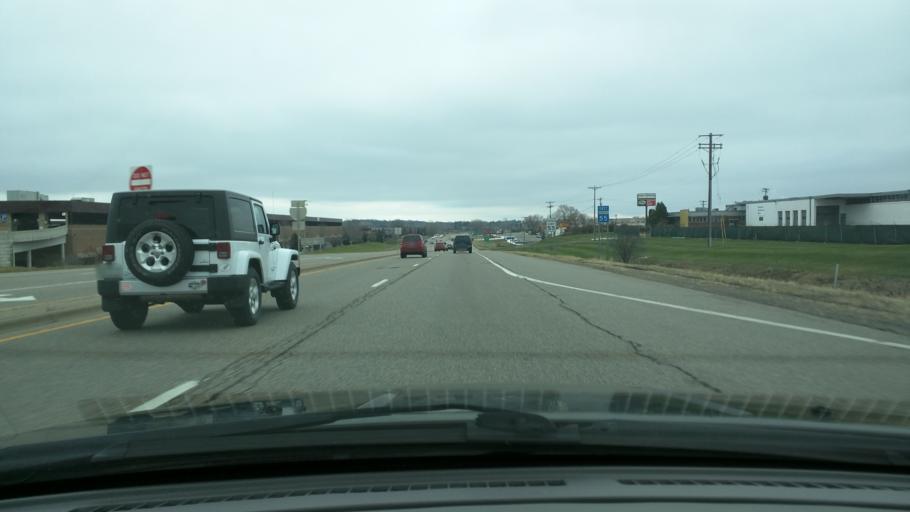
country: US
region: Minnesota
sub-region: Dakota County
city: Mendota Heights
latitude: 44.8580
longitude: -93.1439
